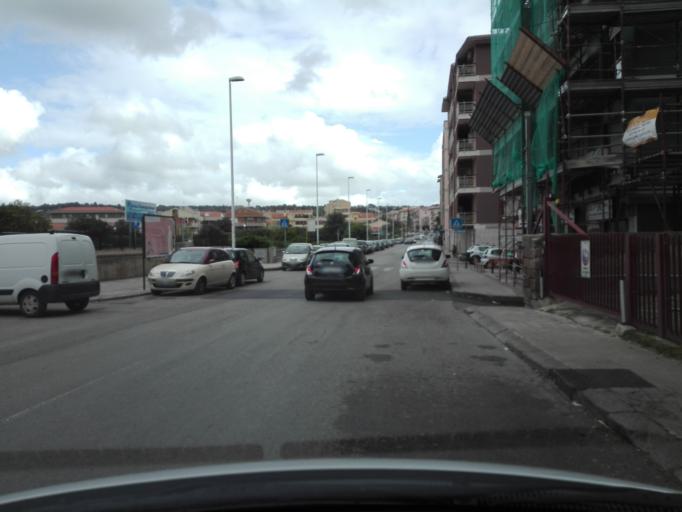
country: IT
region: Sardinia
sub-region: Provincia di Sassari
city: Sassari
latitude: 40.7242
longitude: 8.5776
